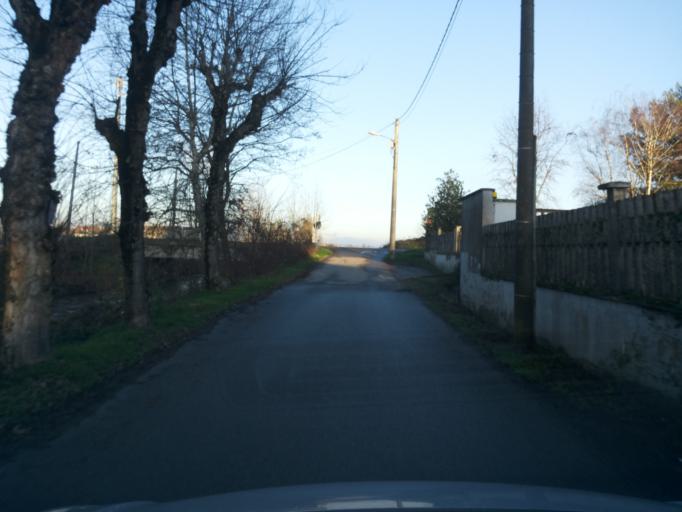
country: IT
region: Piedmont
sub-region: Provincia di Vercelli
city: Asigliano Vercellese
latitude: 45.2609
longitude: 8.4143
